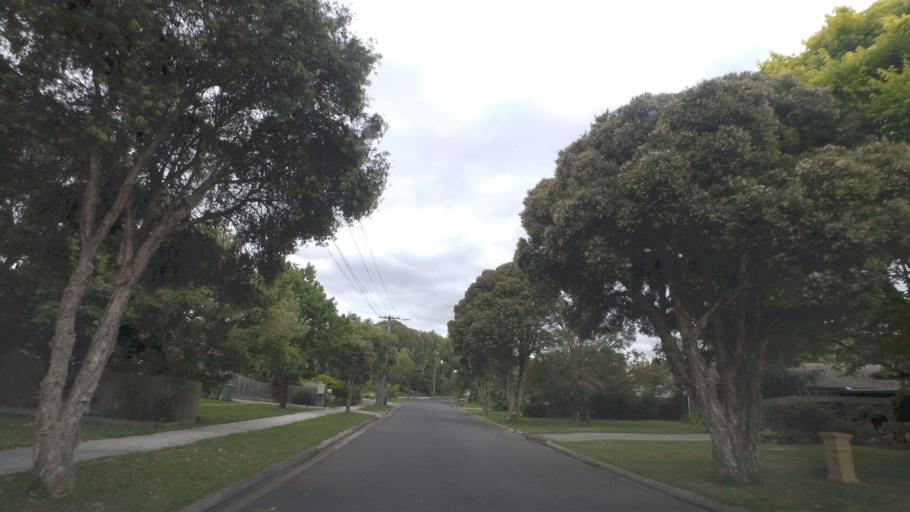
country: AU
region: Victoria
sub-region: Yarra Ranges
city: Lilydale
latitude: -37.7494
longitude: 145.3427
